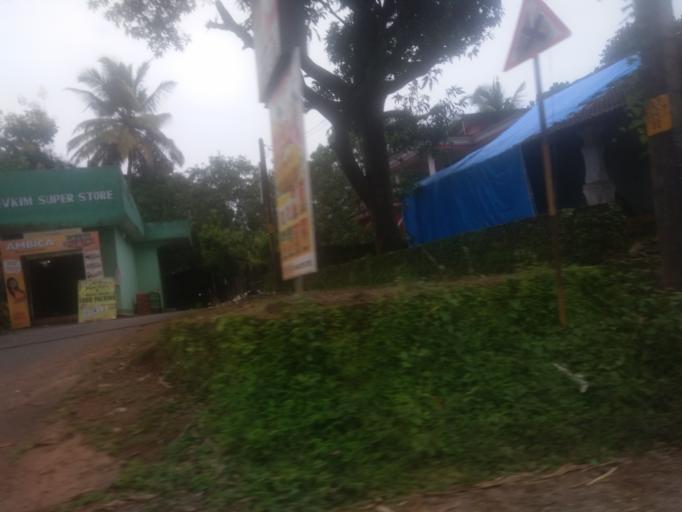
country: IN
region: Goa
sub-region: South Goa
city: Chinchinim
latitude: 15.2137
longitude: 73.9729
